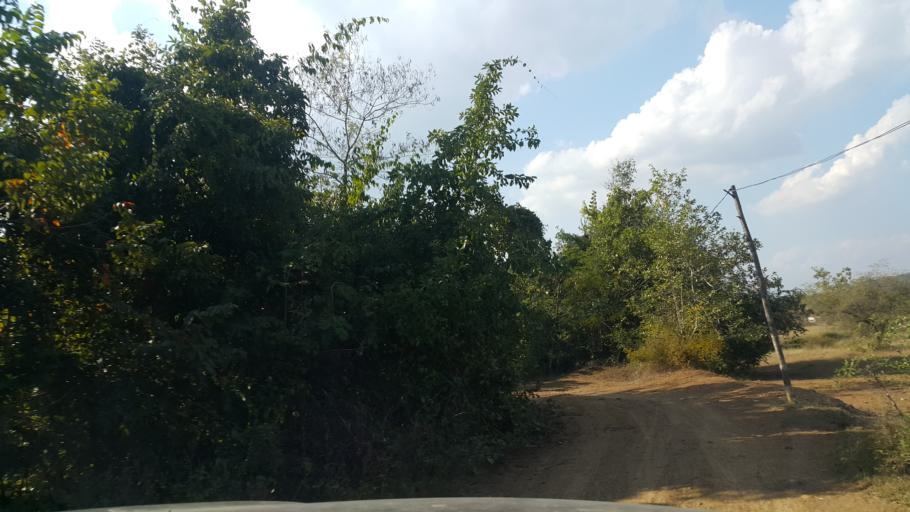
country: TH
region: Lamphun
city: Ban Thi
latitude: 18.5649
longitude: 99.1223
